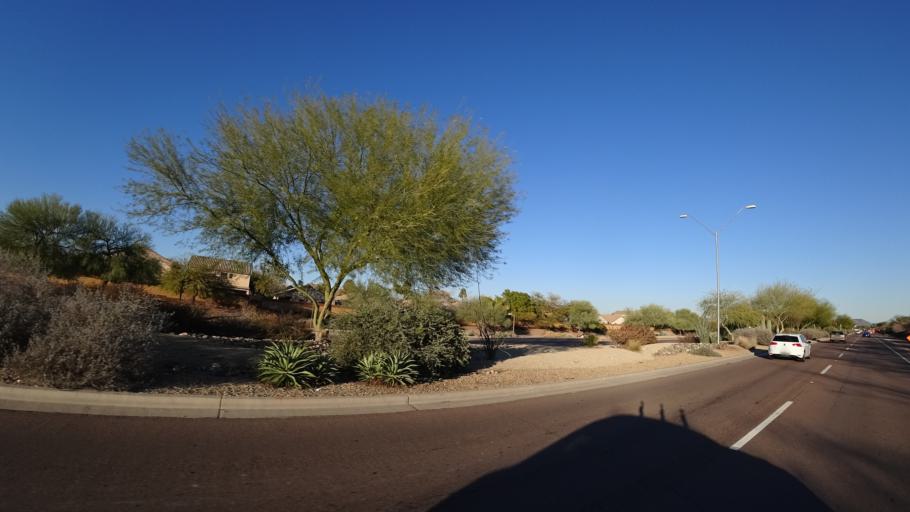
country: US
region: Arizona
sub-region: Maricopa County
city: Sun City
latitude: 33.6744
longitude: -112.2615
